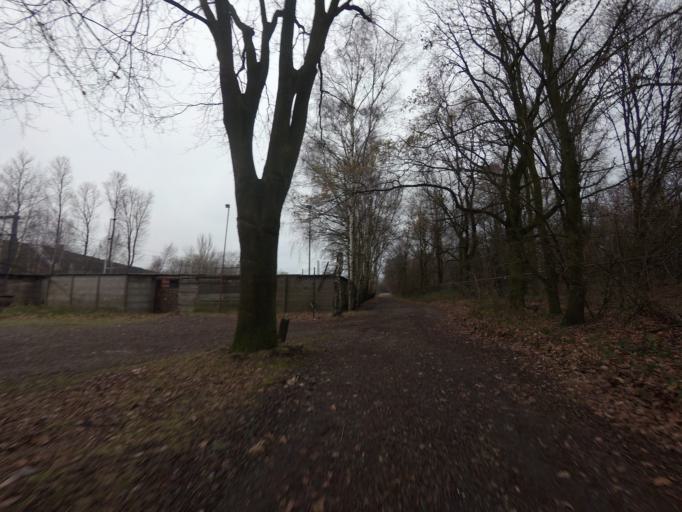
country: BE
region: Flanders
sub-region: Provincie Antwerpen
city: Hoboken
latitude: 51.1636
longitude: 4.3435
